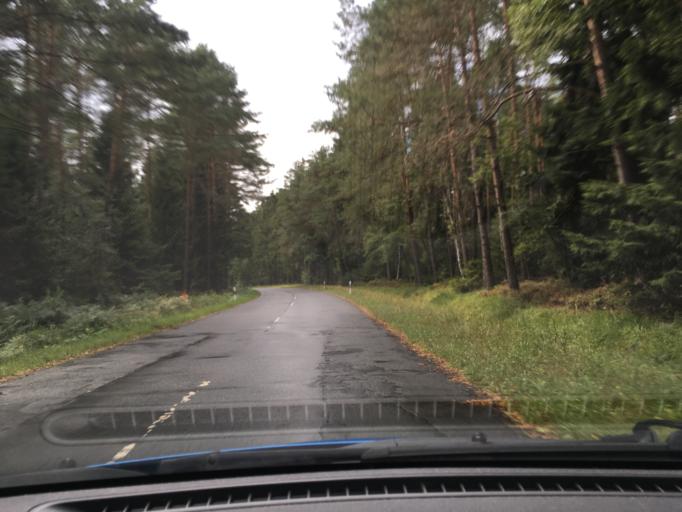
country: DE
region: Lower Saxony
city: Wietzendorf
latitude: 52.9850
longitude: 9.9615
